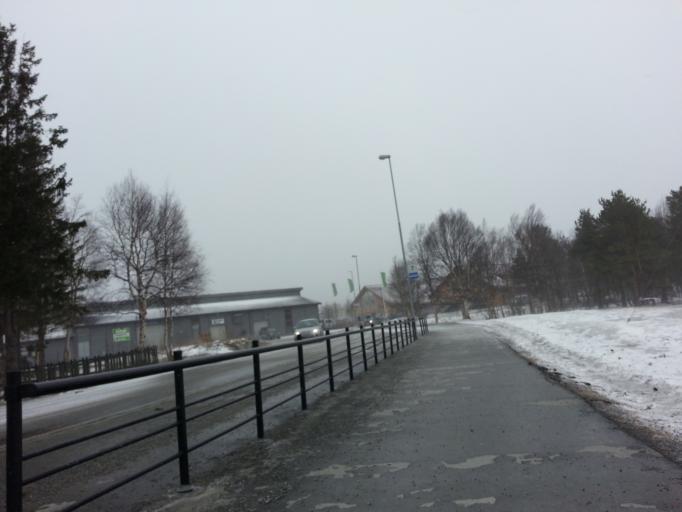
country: NO
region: Sor-Trondelag
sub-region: Oppdal
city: Oppdal
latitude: 62.5939
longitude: 9.6849
